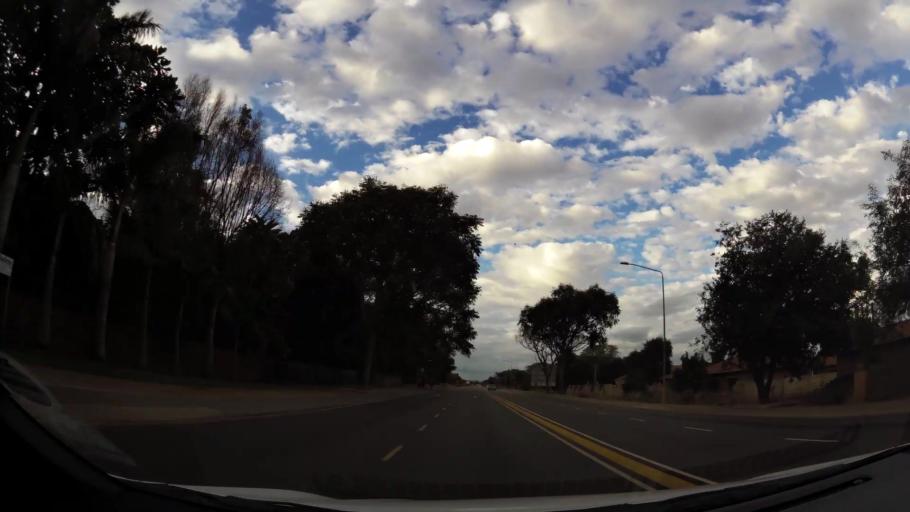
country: ZA
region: Limpopo
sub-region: Waterberg District Municipality
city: Modimolle
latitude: -24.5107
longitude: 28.7232
